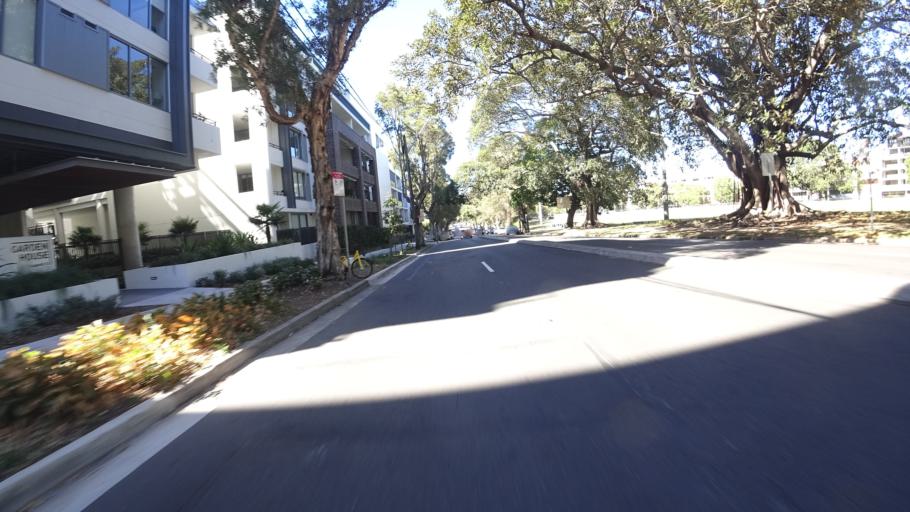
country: AU
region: New South Wales
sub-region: City of Sydney
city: Alexandria
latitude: -33.9007
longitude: 151.2062
